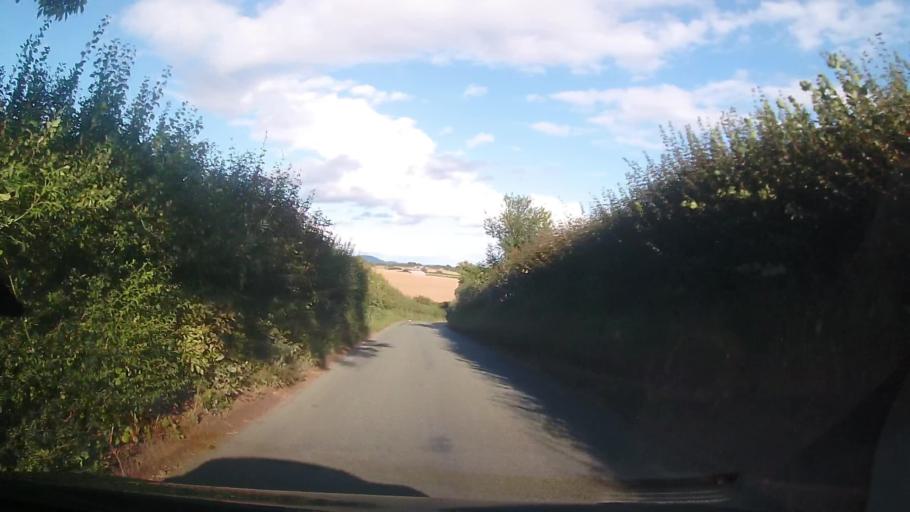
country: GB
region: England
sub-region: Shropshire
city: Great Hanwood
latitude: 52.6505
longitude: -2.7940
